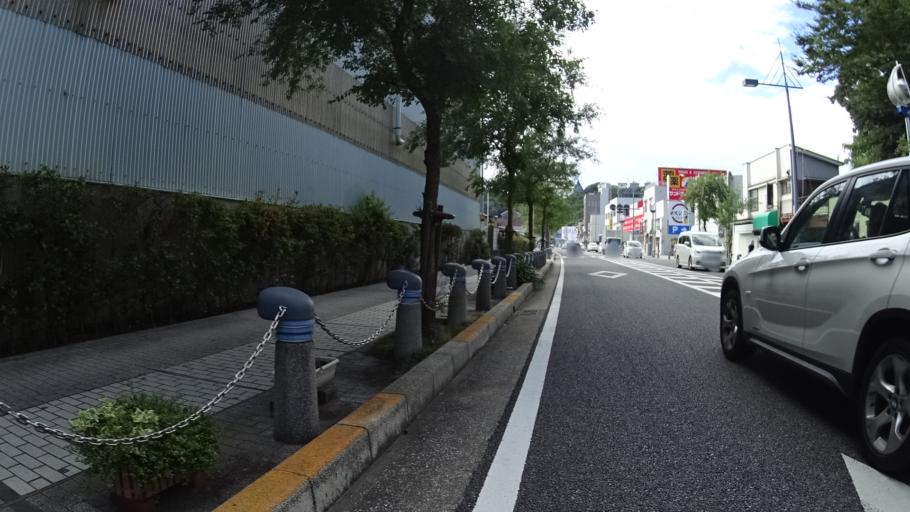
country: JP
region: Kanagawa
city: Yokosuka
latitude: 35.2489
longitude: 139.7150
